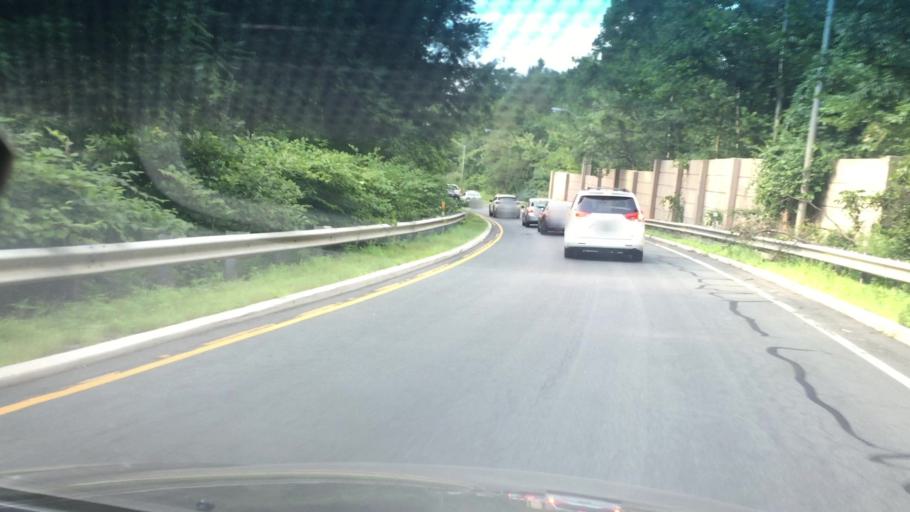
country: US
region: New Jersey
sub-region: Morris County
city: Morris Plains
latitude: 40.8112
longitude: -74.4448
